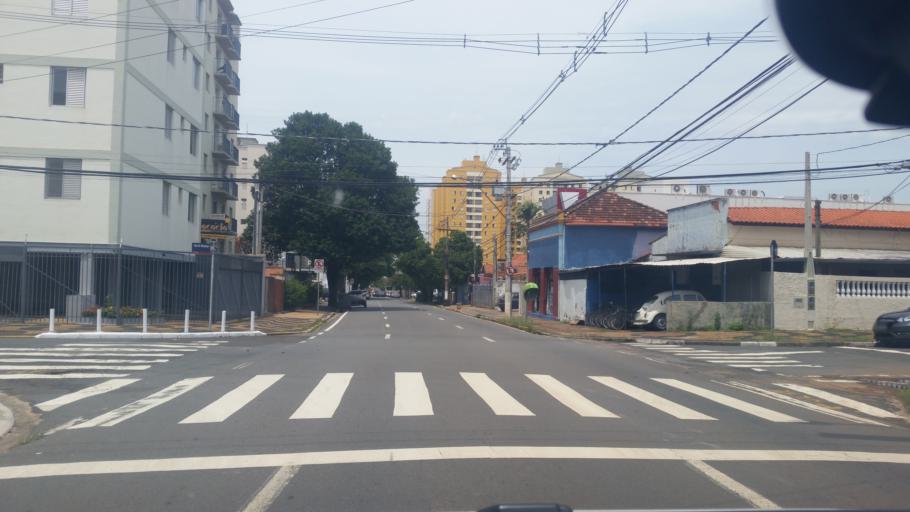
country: BR
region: Sao Paulo
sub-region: Campinas
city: Campinas
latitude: -22.8854
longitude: -47.0639
